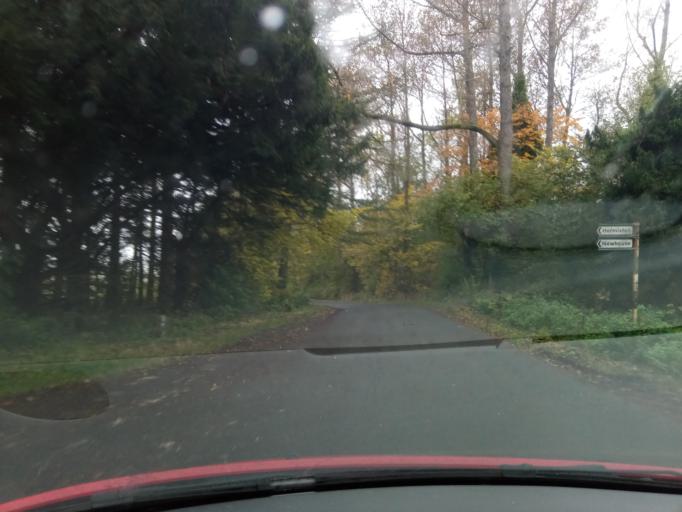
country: GB
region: Scotland
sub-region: The Scottish Borders
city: Selkirk
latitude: 55.5079
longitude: -2.7616
